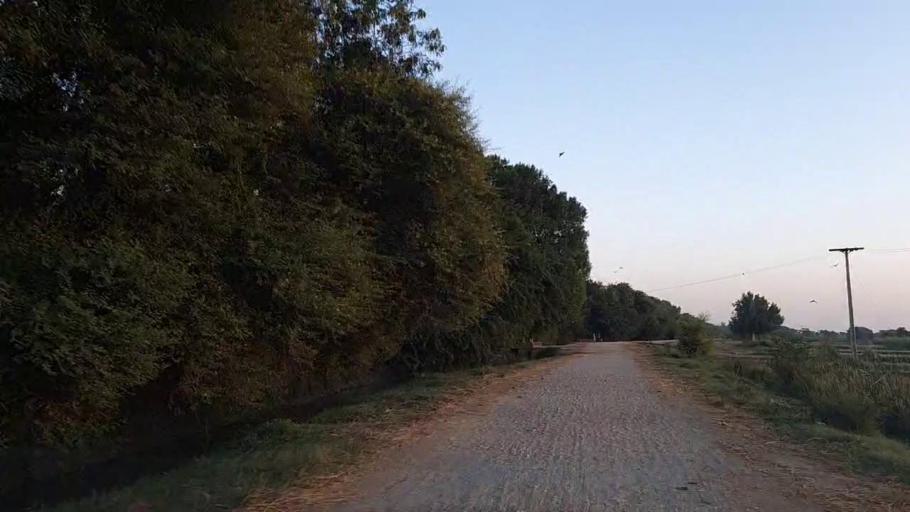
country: PK
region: Sindh
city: Mirpur Batoro
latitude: 24.6397
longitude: 68.1898
